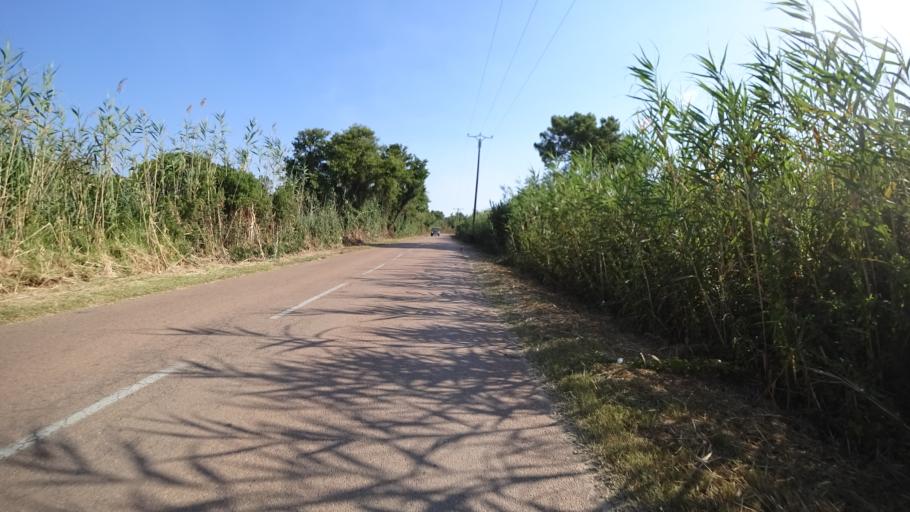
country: FR
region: Corsica
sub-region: Departement de la Corse-du-Sud
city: Porto-Vecchio
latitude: 41.6222
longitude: 9.3337
